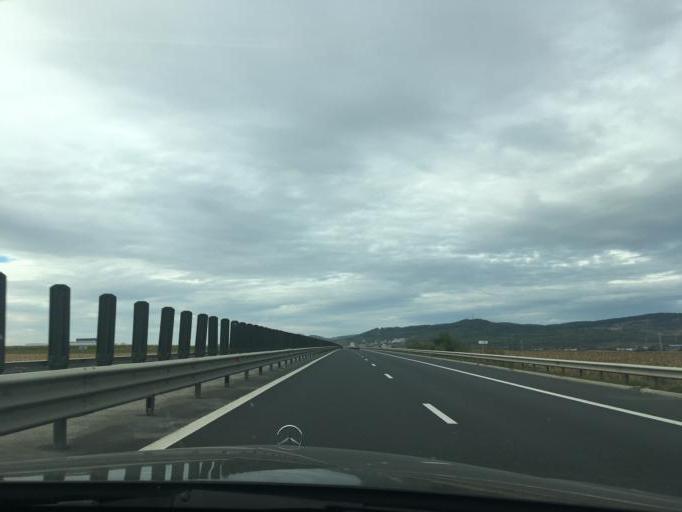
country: RO
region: Sibiu
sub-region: Comuna Selimbar
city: Selimbar
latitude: 45.7720
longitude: 24.2048
